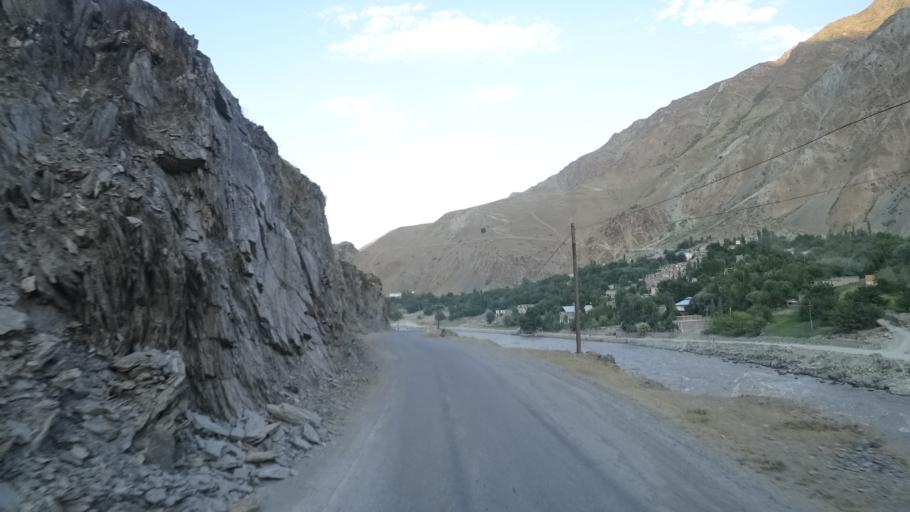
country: AF
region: Badakhshan
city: Nusay
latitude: 38.4451
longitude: 70.8116
